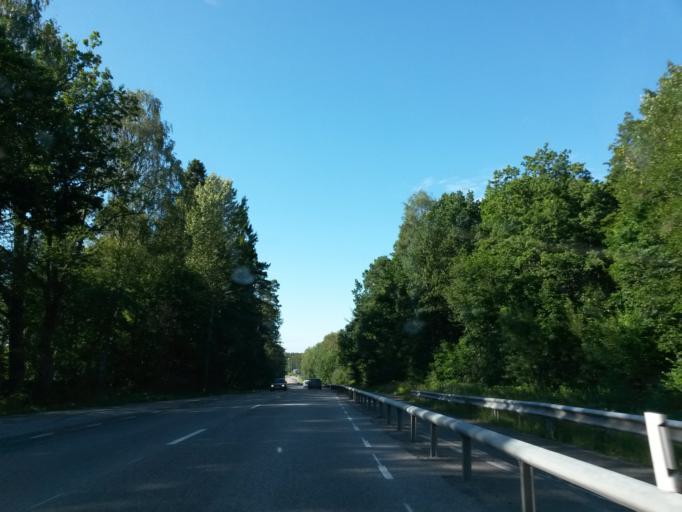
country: SE
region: Vaestra Goetaland
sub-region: Boras Kommun
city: Ganghester
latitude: 57.8004
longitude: 13.0115
